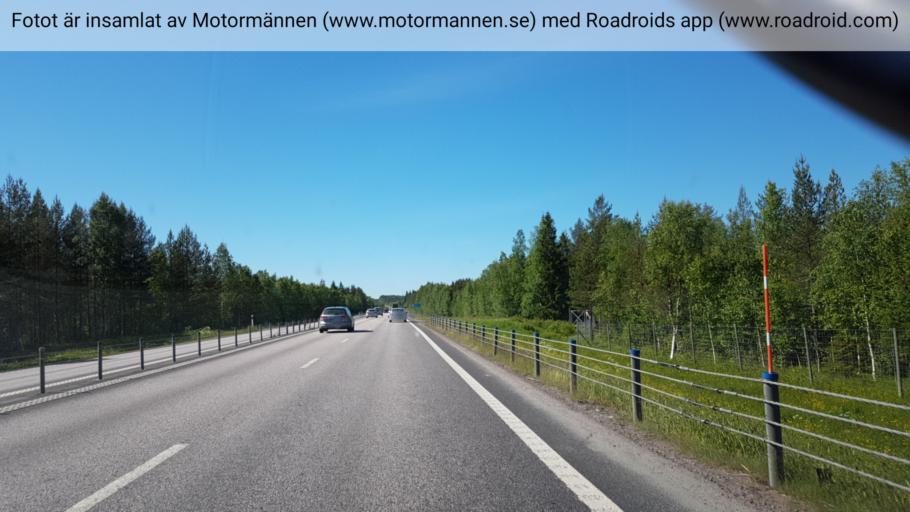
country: SE
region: Norrbotten
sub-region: Pitea Kommun
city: Rosvik
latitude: 65.4814
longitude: 21.7402
